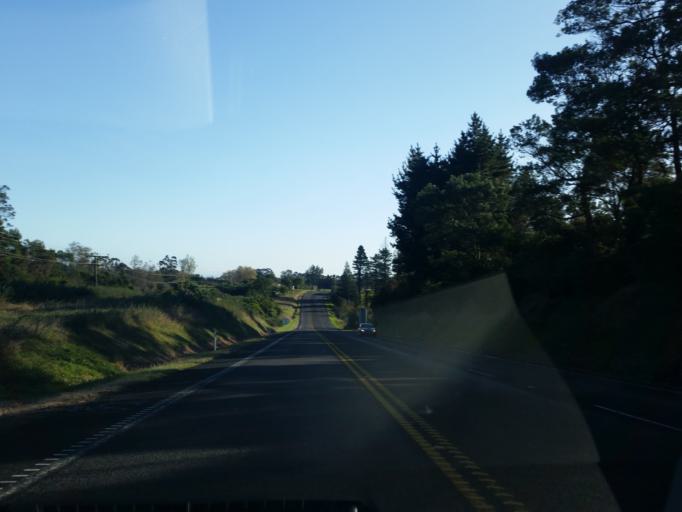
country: NZ
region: Bay of Plenty
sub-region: Western Bay of Plenty District
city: Katikati
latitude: -37.6431
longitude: 175.9643
